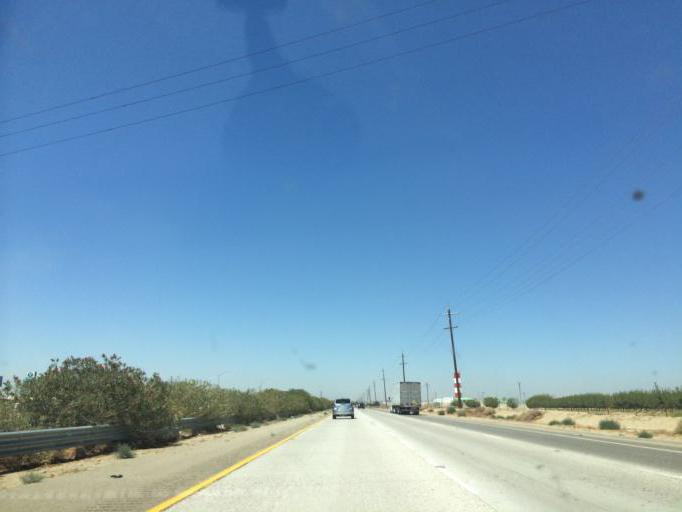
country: US
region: California
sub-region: Kern County
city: Weedpatch
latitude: 35.0759
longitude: -118.9735
